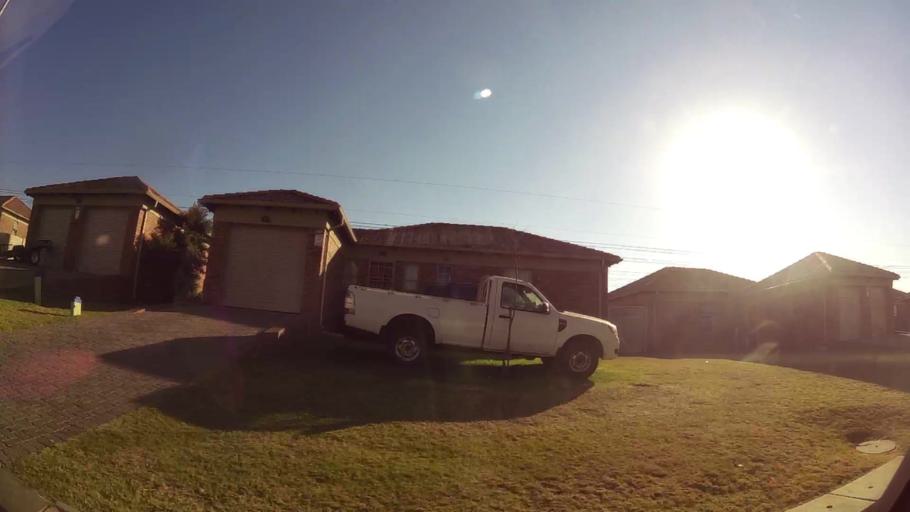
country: ZA
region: Gauteng
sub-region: City of Johannesburg Metropolitan Municipality
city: Midrand
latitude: -25.9073
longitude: 28.1097
